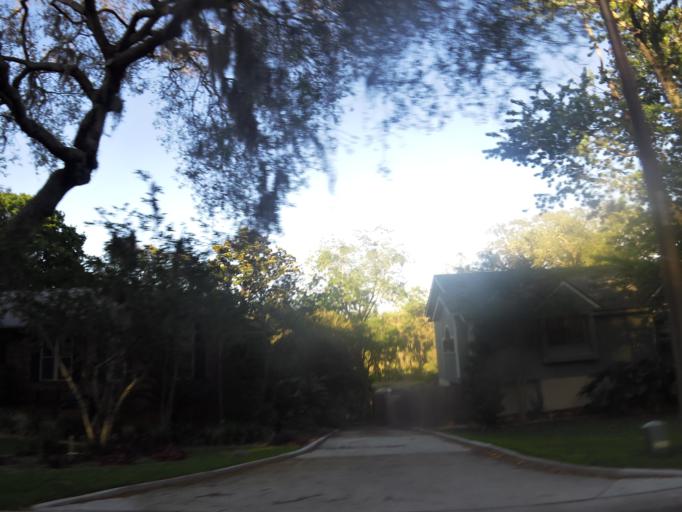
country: US
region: Florida
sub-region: Duval County
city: Atlantic Beach
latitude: 30.3827
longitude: -81.5031
